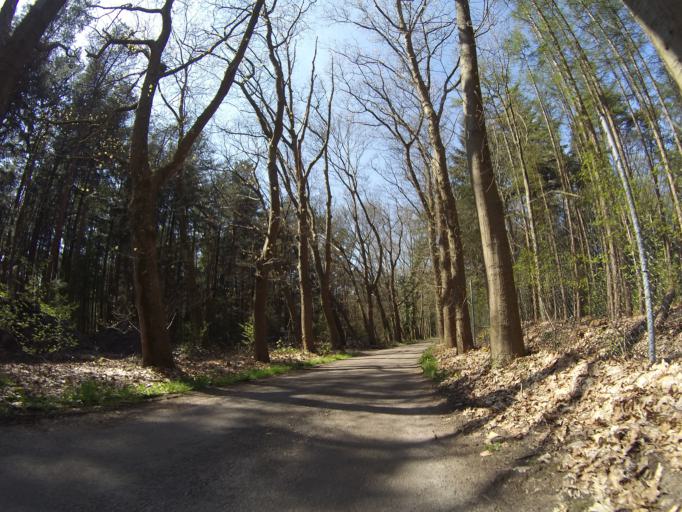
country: NL
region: Utrecht
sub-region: Gemeente Utrechtse Heuvelrug
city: Maarn
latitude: 52.0732
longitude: 5.3632
